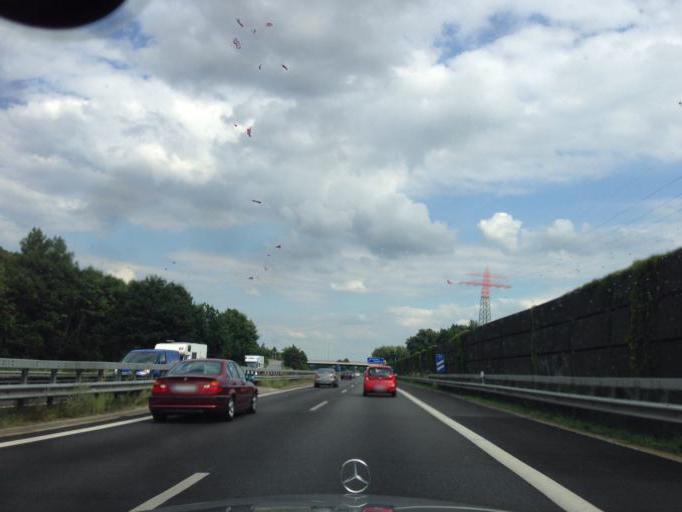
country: DE
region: Hamburg
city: Bergedorf
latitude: 53.4747
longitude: 10.1709
